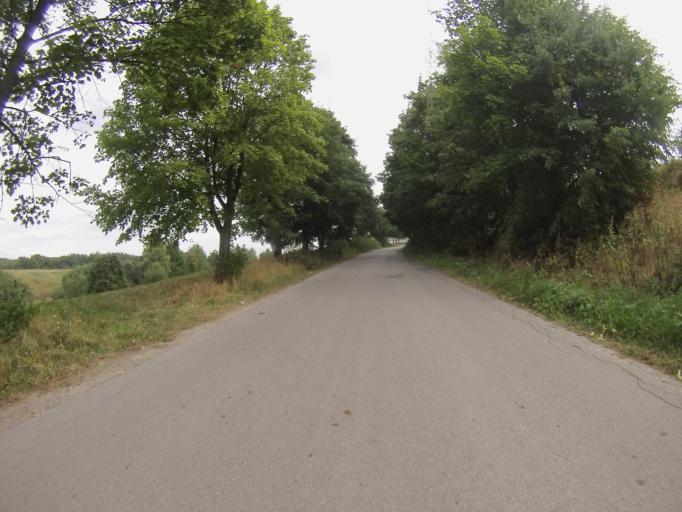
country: PL
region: Swietokrzyskie
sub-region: Powiat kielecki
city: Lagow
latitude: 50.7216
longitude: 21.1130
